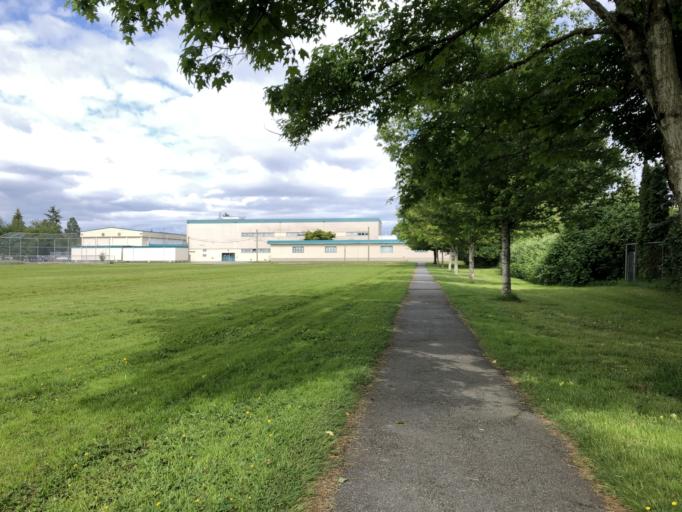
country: CA
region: British Columbia
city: Richmond
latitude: 49.1520
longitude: -123.1282
